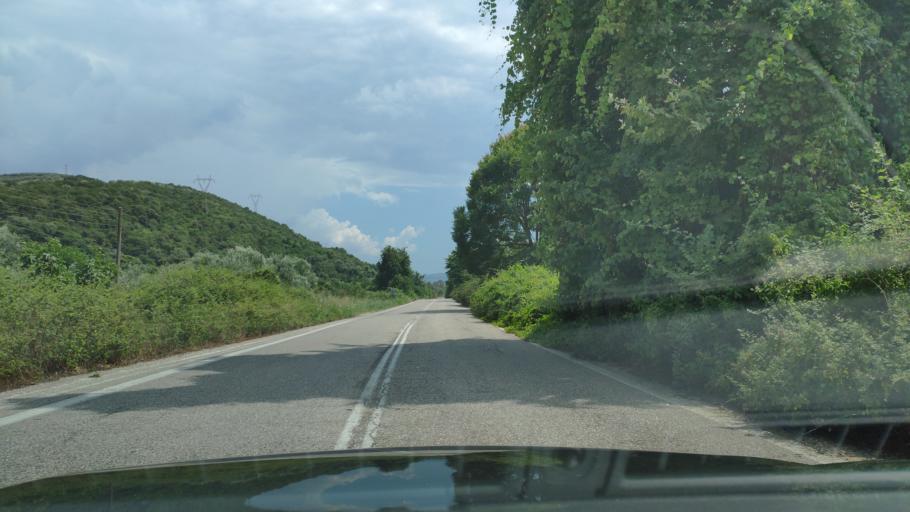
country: GR
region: West Greece
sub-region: Nomos Aitolias kai Akarnanias
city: Krikellos
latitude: 38.9884
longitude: 21.1613
